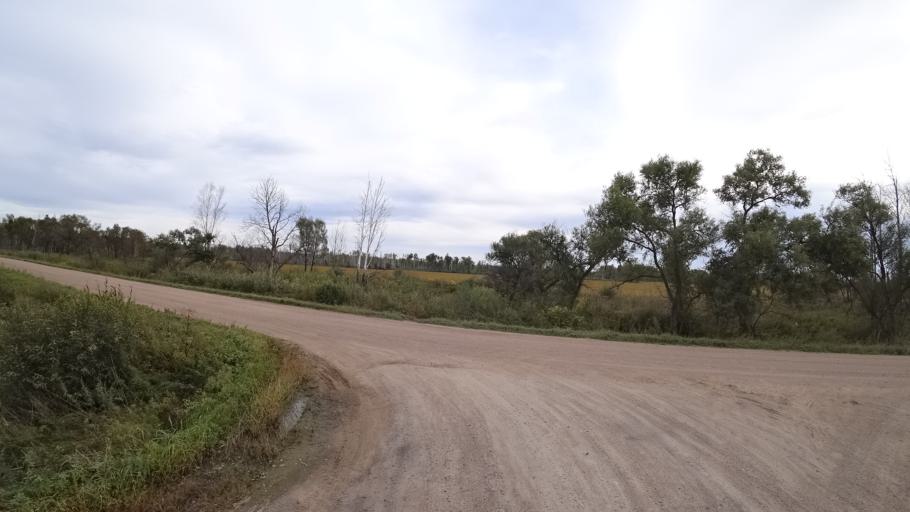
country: RU
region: Amur
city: Arkhara
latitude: 49.3734
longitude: 130.2053
